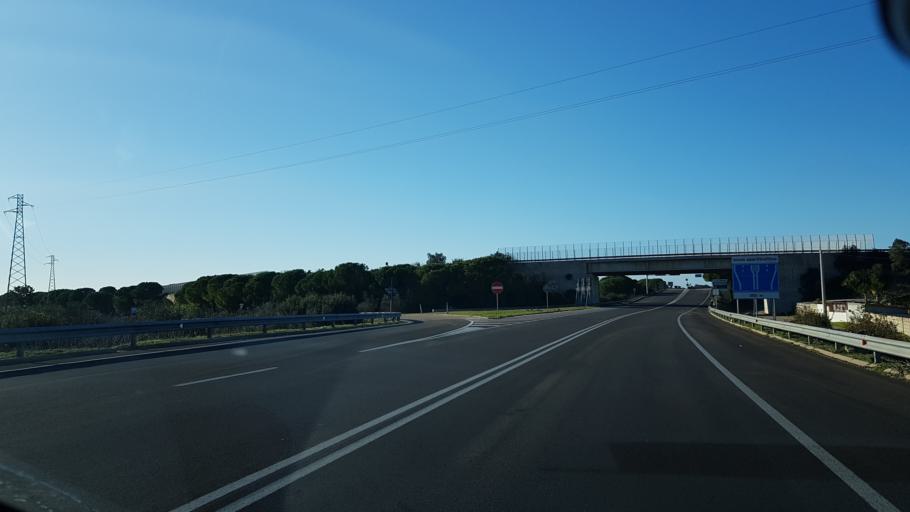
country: IT
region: Apulia
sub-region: Provincia di Lecce
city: Taviano
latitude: 39.9998
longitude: 18.0675
